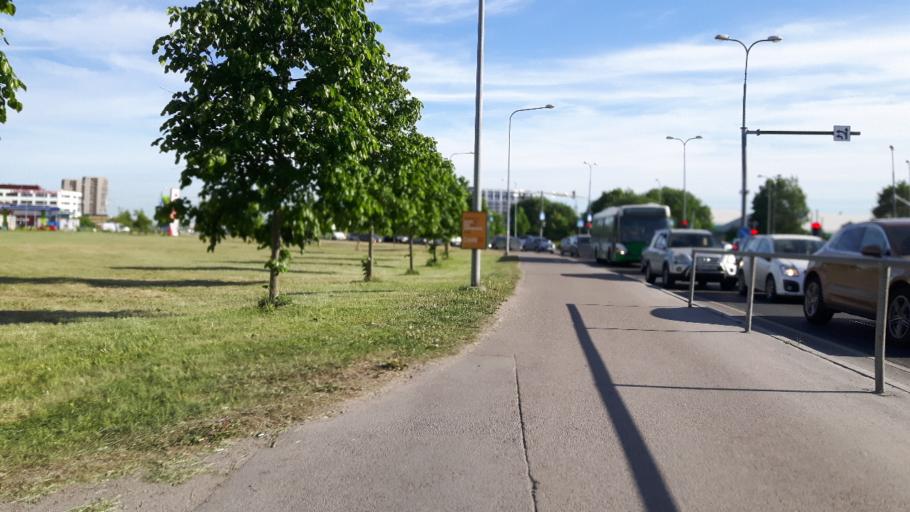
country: EE
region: Harju
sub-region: Tallinna linn
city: Kose
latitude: 59.4523
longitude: 24.8594
